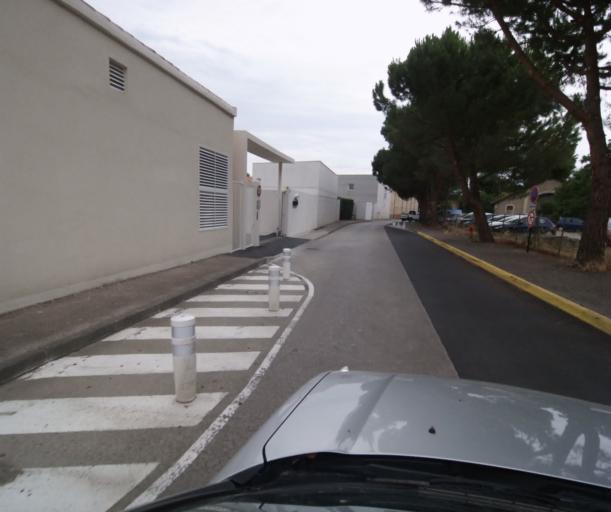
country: FR
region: Languedoc-Roussillon
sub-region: Departement de l'Aude
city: Limoux
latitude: 43.0553
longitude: 2.2227
